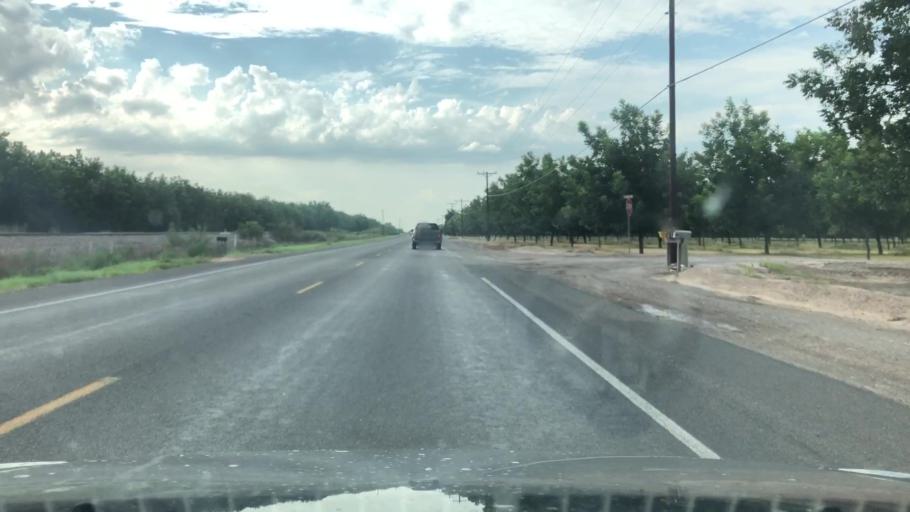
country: US
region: New Mexico
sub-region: Dona Ana County
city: Mesquite
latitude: 32.2139
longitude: -106.7276
